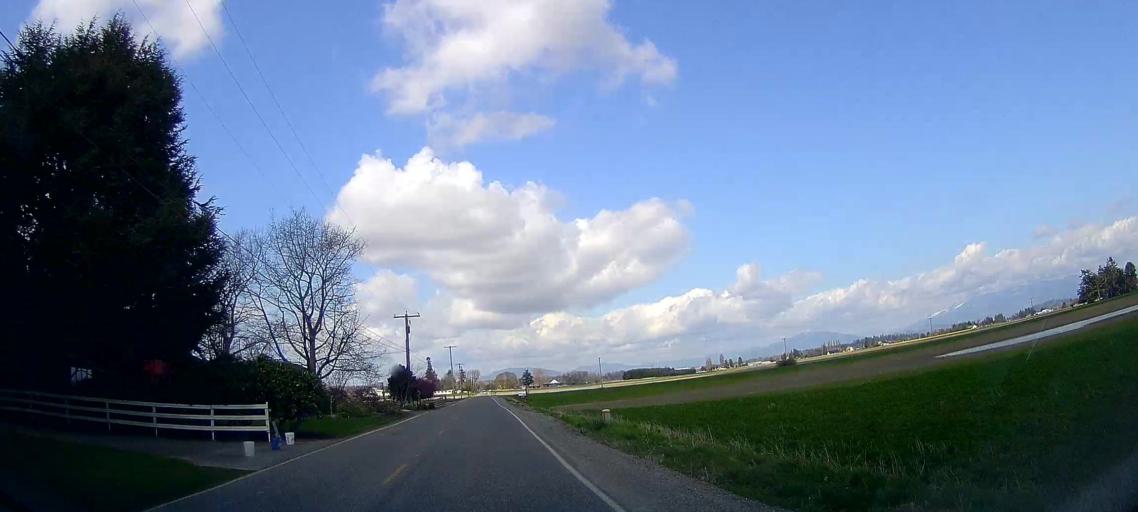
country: US
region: Washington
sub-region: Skagit County
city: Mount Vernon
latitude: 48.4300
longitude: -122.4219
